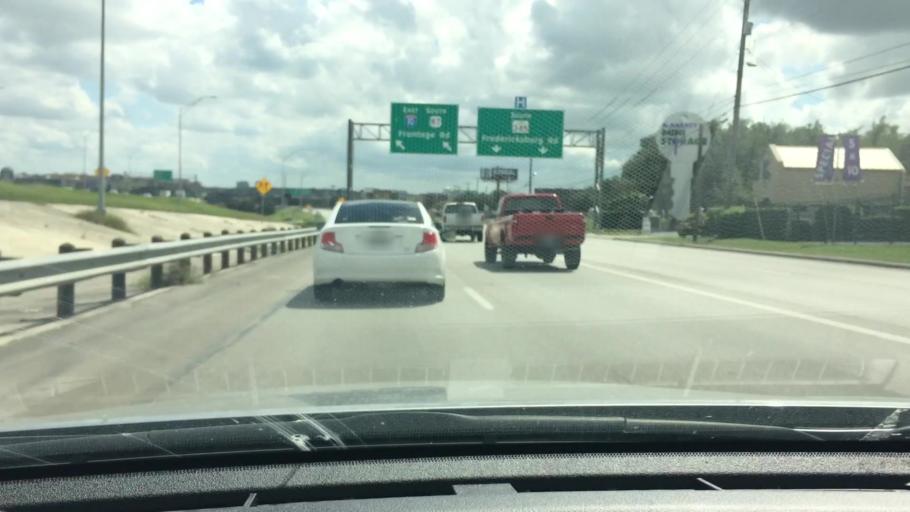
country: US
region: Texas
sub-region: Bexar County
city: Shavano Park
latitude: 29.5533
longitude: -98.5871
